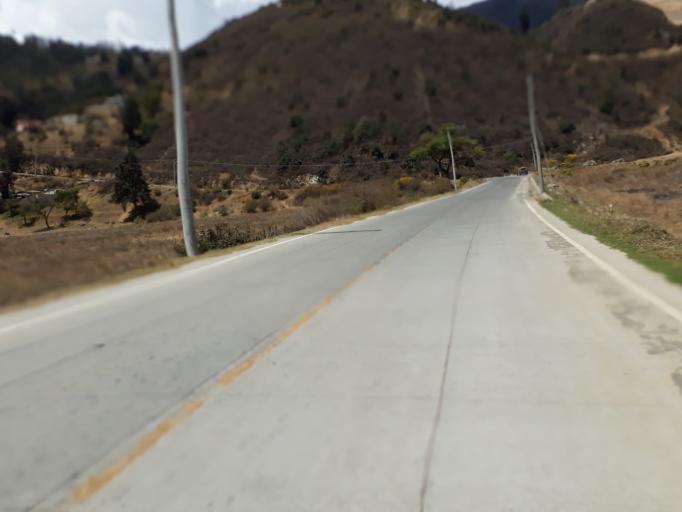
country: GT
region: Quetzaltenango
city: Quetzaltenango
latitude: 14.8155
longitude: -91.5541
